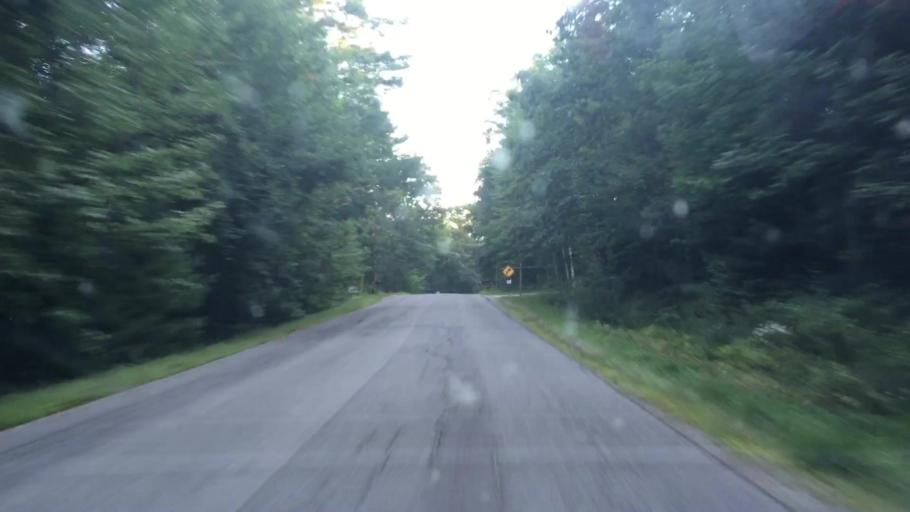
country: US
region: Maine
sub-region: Waldo County
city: Frankfort
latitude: 44.6634
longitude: -68.9275
